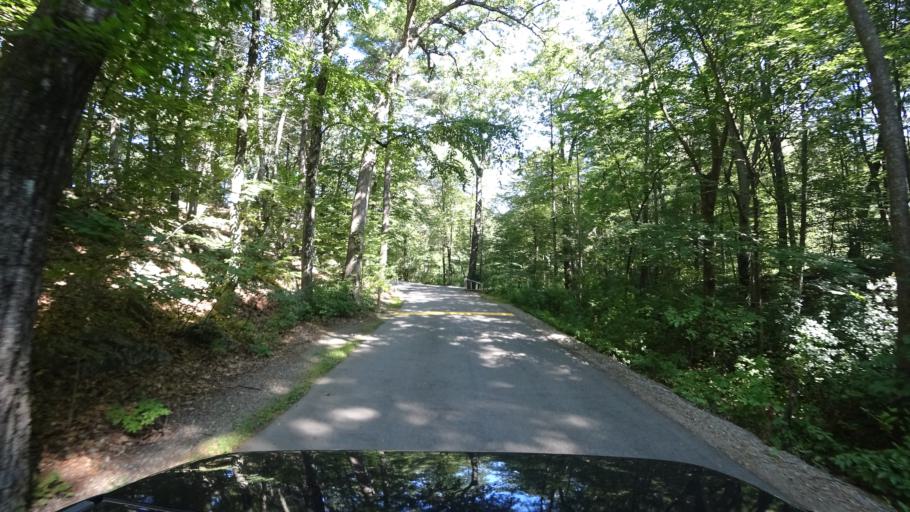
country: US
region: Massachusetts
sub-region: Norfolk County
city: Dedham
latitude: 42.2583
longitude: -71.1824
